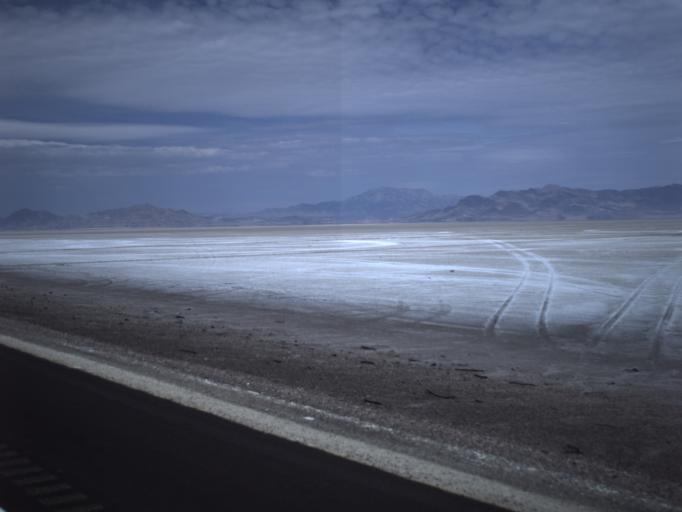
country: US
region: Utah
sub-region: Tooele County
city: Wendover
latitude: 40.7352
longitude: -113.6491
